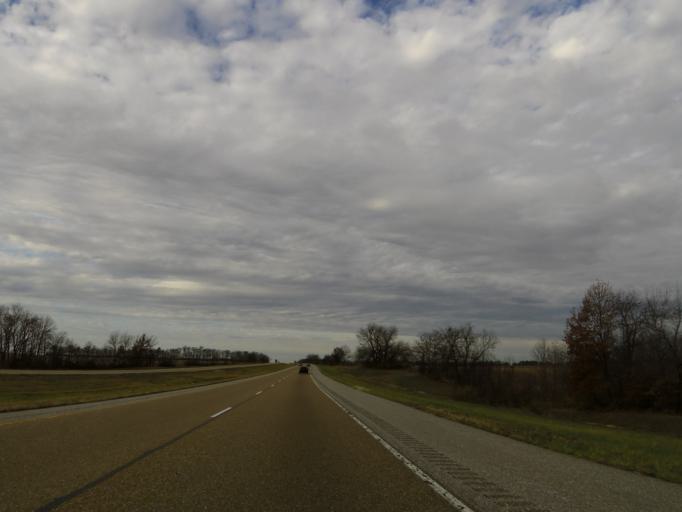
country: US
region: Illinois
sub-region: Clinton County
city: Wamac
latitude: 38.3893
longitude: -89.2194
